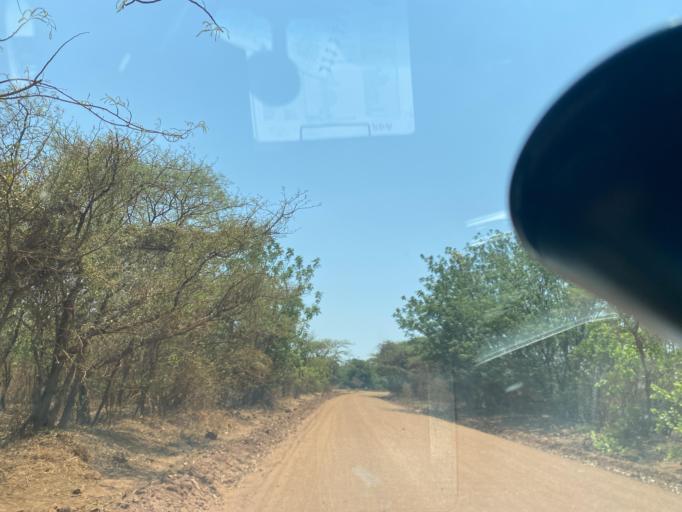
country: ZM
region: Southern
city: Nakambala
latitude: -15.4957
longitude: 27.9076
